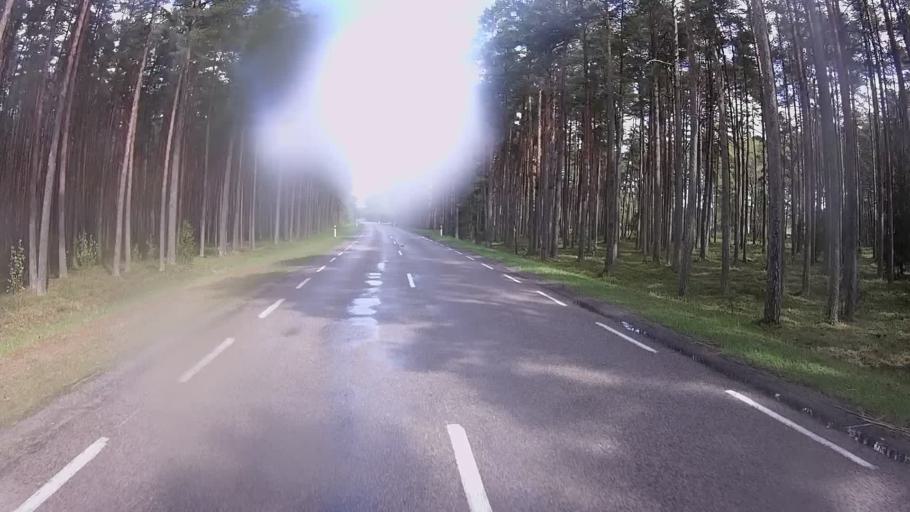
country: EE
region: Hiiumaa
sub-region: Kaerdla linn
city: Kardla
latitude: 58.7161
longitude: 22.6151
